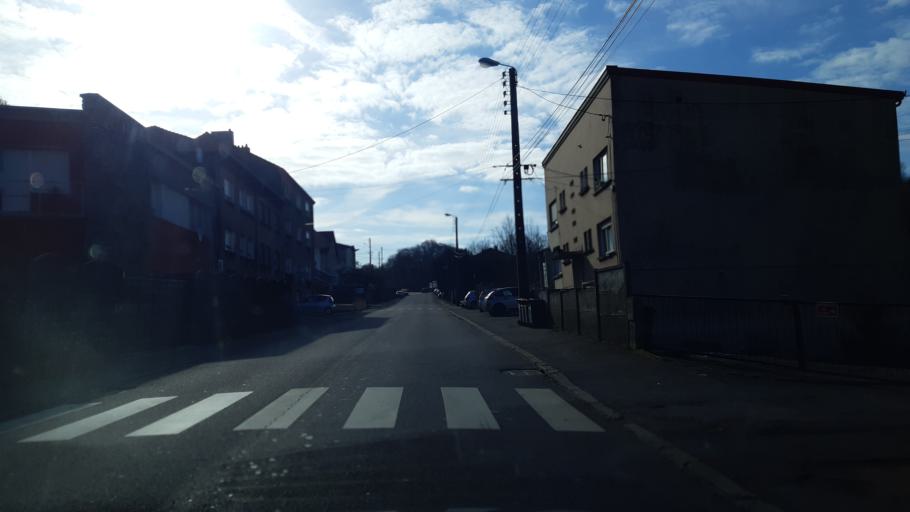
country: FR
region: Lorraine
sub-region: Departement de la Moselle
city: Audun-le-Tiche
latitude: 49.4667
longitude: 5.9575
